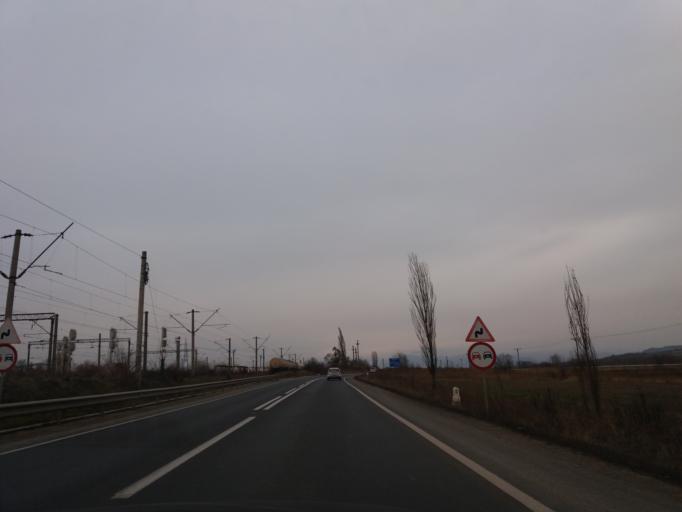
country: RO
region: Hunedoara
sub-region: Comuna Calan
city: Calan
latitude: 45.7553
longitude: 23.0007
